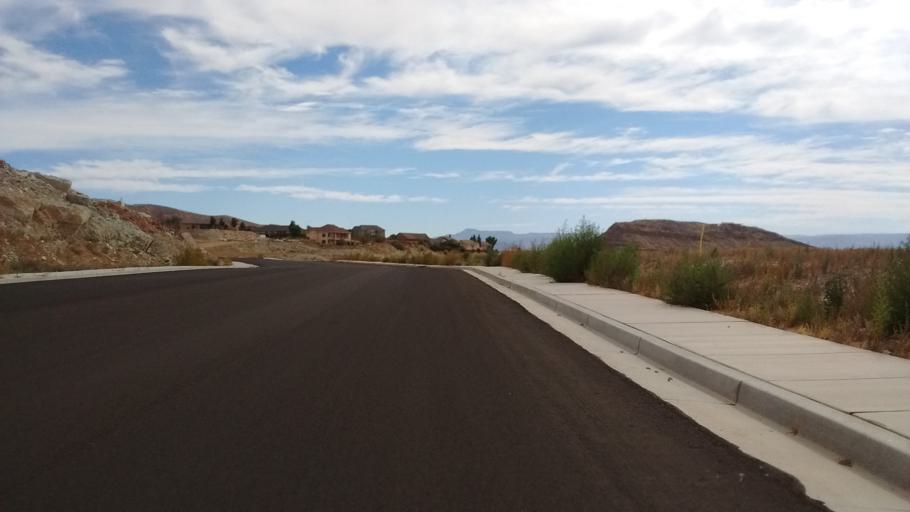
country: US
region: Utah
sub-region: Washington County
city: Washington
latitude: 37.1160
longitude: -113.4945
